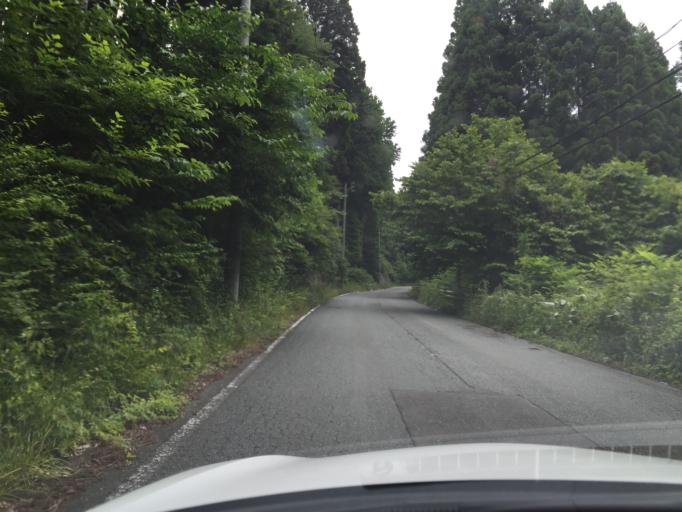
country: JP
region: Fukushima
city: Iwaki
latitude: 37.1445
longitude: 140.7010
